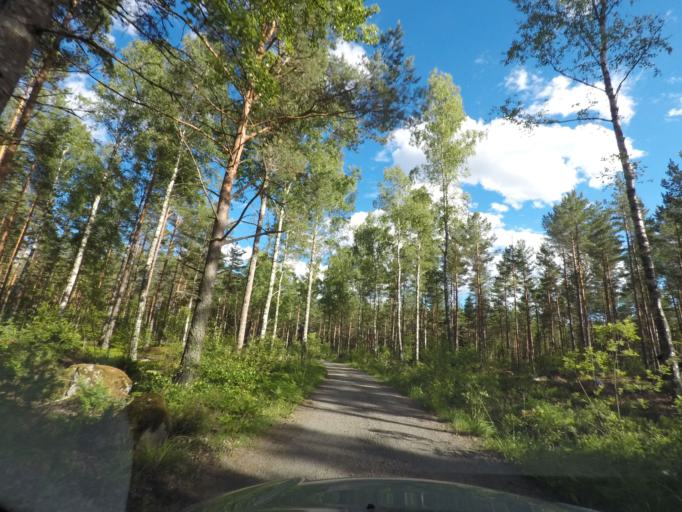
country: SE
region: Stockholm
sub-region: Sigtuna Kommun
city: Marsta
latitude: 59.6970
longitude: 17.9454
